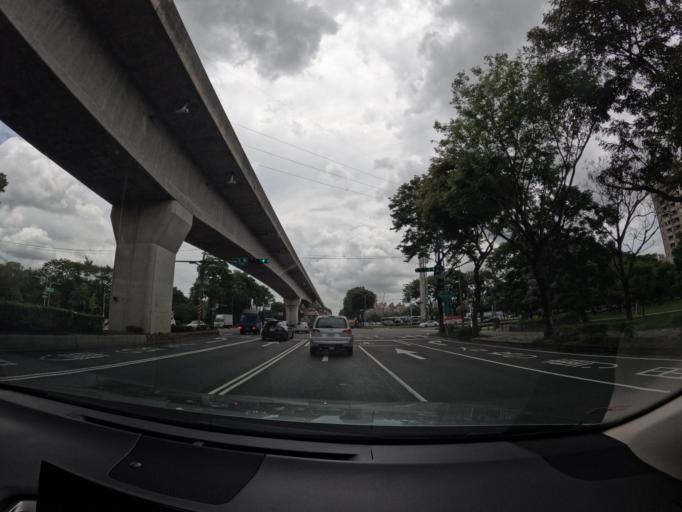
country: TW
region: Taiwan
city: Fengshan
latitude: 22.7335
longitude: 120.3196
